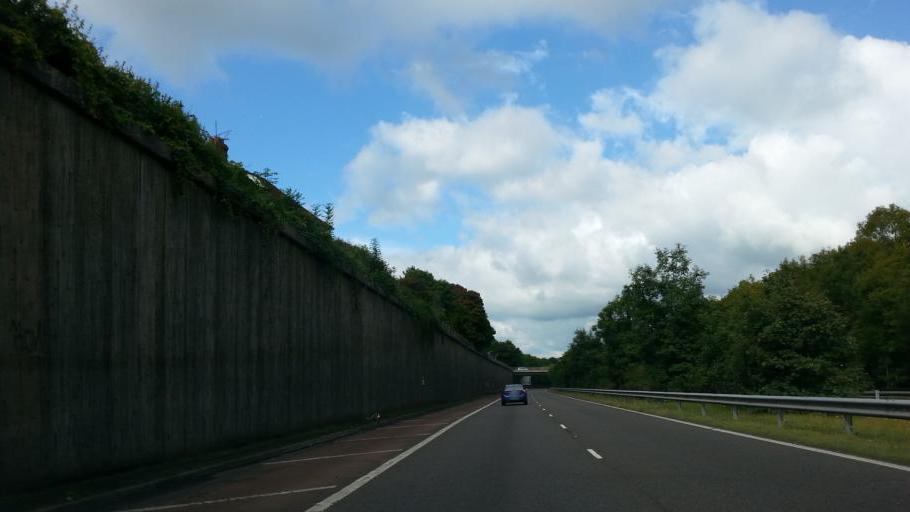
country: GB
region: England
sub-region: Wokingham
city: Earley
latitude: 51.4442
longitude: -0.9247
